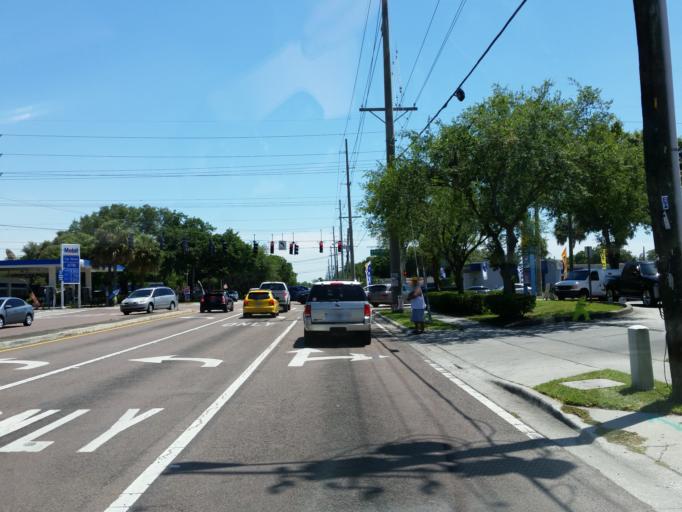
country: US
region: Florida
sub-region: Hillsborough County
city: Riverview
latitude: 27.8942
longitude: -82.2940
